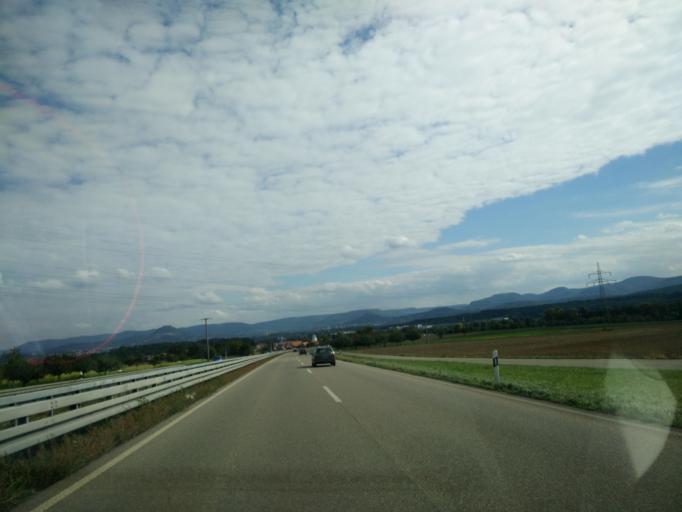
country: DE
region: Baden-Wuerttemberg
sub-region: Tuebingen Region
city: Kusterdingen
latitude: 48.5054
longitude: 9.1136
